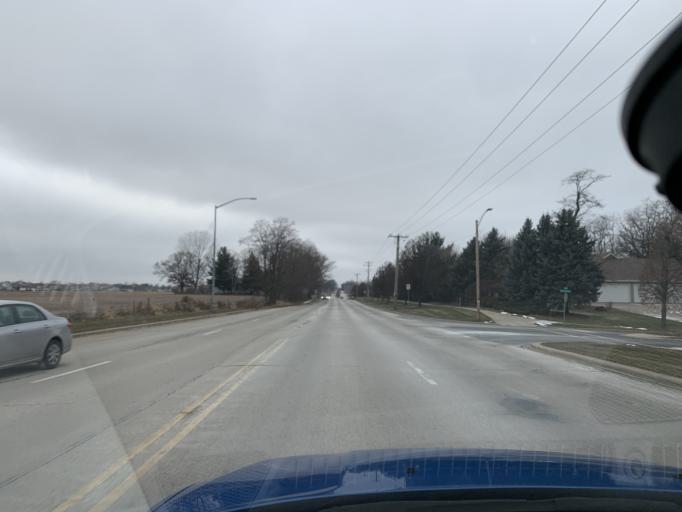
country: US
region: Wisconsin
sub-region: Dane County
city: Middleton
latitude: 43.0748
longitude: -89.5396
